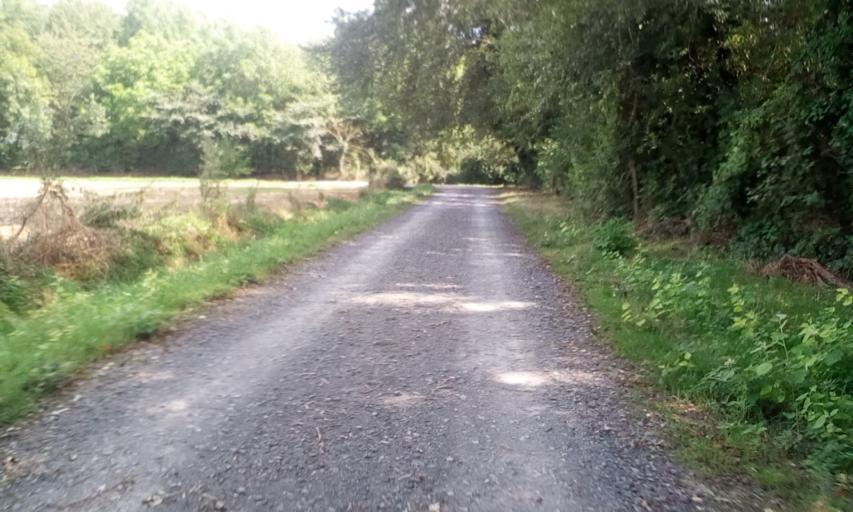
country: FR
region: Lower Normandy
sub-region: Departement du Calvados
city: Argences
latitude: 49.1413
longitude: -0.1673
